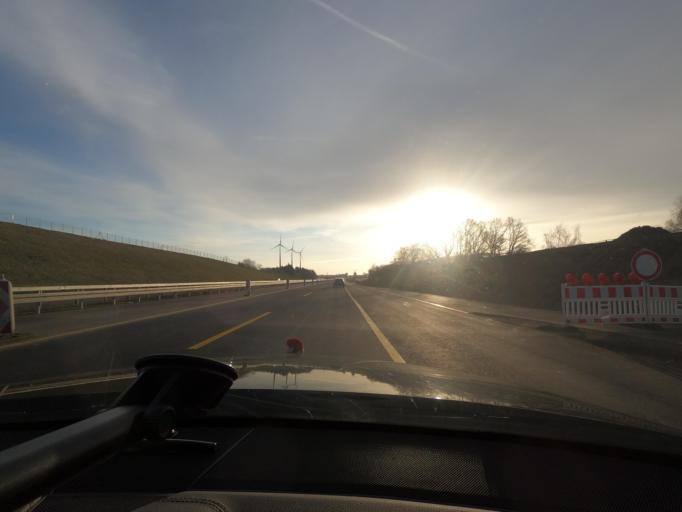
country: DE
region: Lower Saxony
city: Seesen
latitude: 51.8426
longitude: 10.1202
